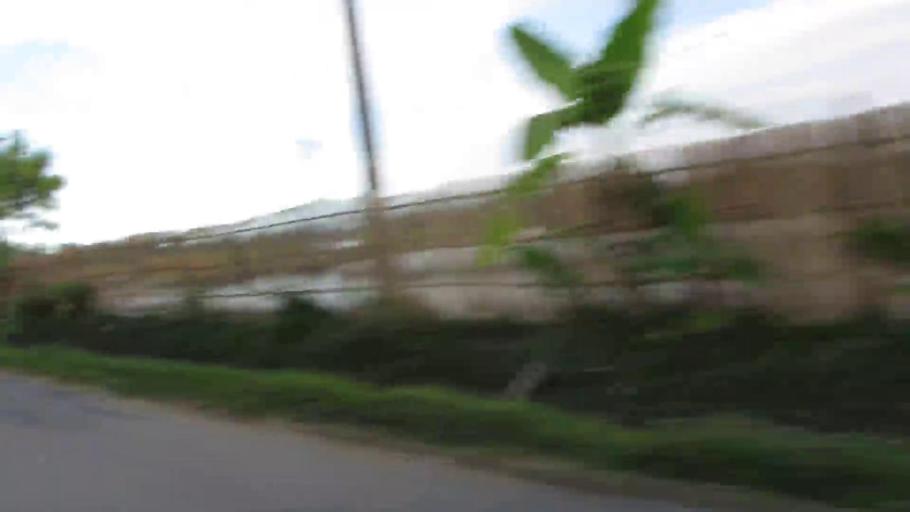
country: ID
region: West Java
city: Karangjaladri
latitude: -7.7121
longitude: 108.4981
